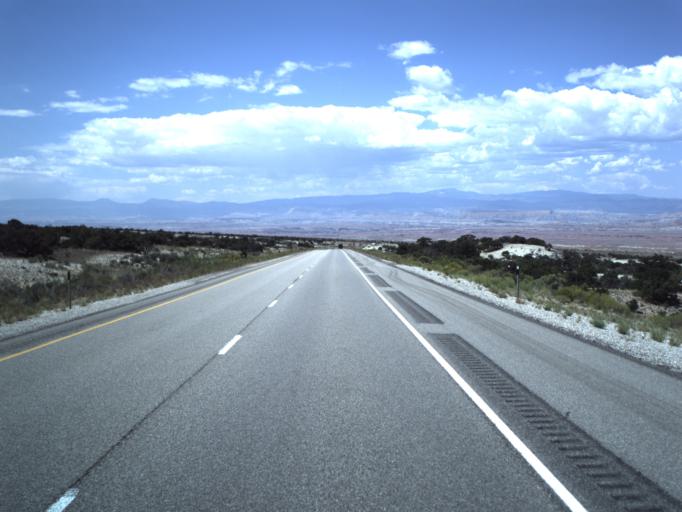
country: US
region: Utah
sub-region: Emery County
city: Ferron
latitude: 38.8459
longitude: -110.9447
